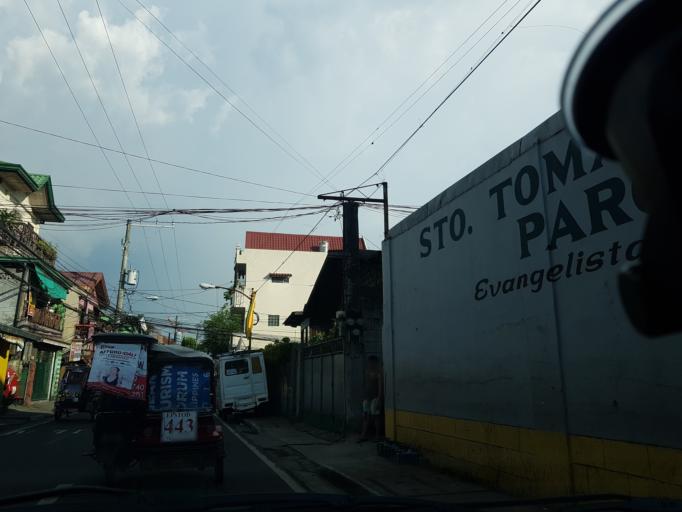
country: PH
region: Metro Manila
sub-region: Marikina
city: Calumpang
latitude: 14.6136
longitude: 121.0833
